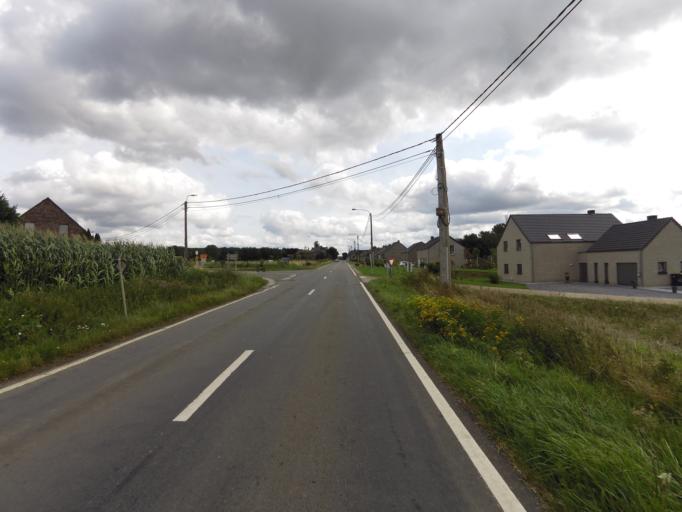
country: BE
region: Wallonia
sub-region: Province de Liege
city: Clavier
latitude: 50.4275
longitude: 5.3525
